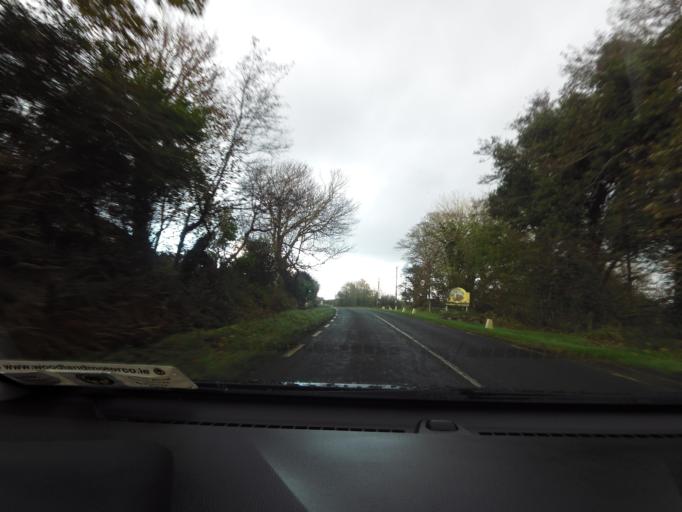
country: IE
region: Connaught
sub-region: Maigh Eo
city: Westport
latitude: 53.7668
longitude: -9.7856
